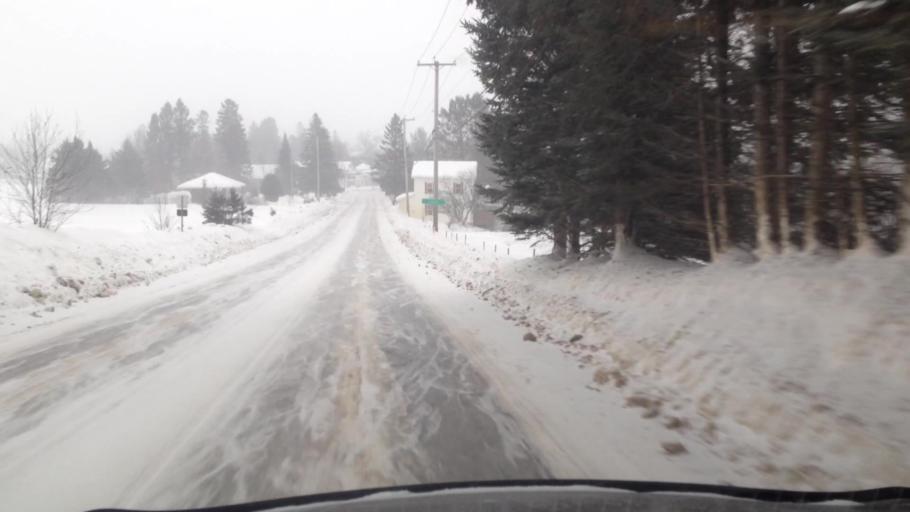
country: CA
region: Quebec
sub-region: Laurentides
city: Mont-Tremblant
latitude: 45.9675
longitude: -74.6210
